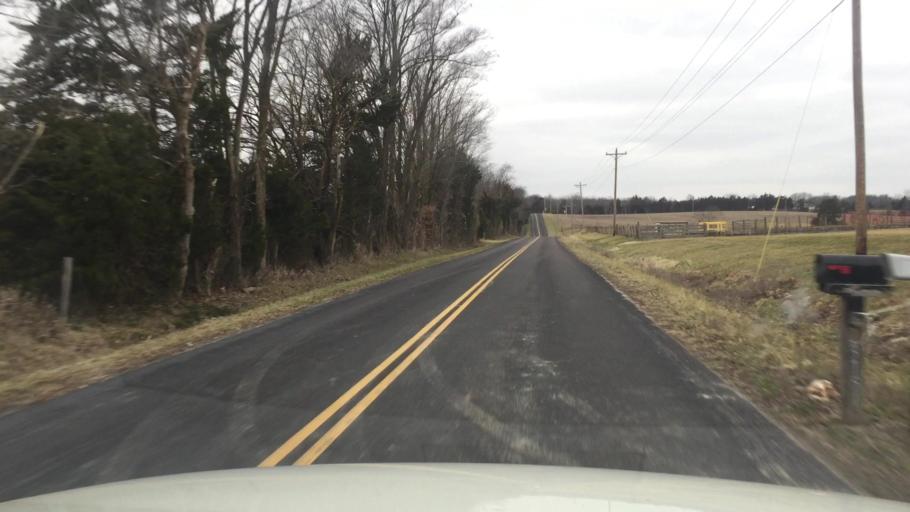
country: US
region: Missouri
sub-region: Boone County
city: Ashland
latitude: 38.8149
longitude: -92.2861
